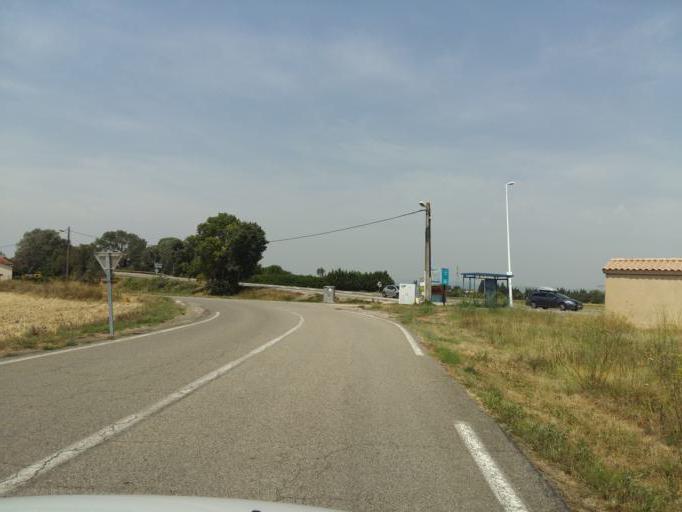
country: FR
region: Provence-Alpes-Cote d'Azur
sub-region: Departement du Vaucluse
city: Mondragon
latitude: 44.2733
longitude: 4.7122
